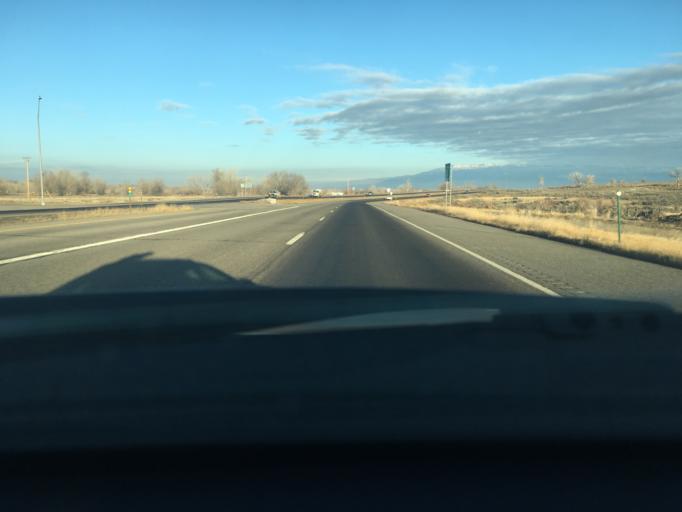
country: US
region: Colorado
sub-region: Montrose County
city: Olathe
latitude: 38.6172
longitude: -107.9824
